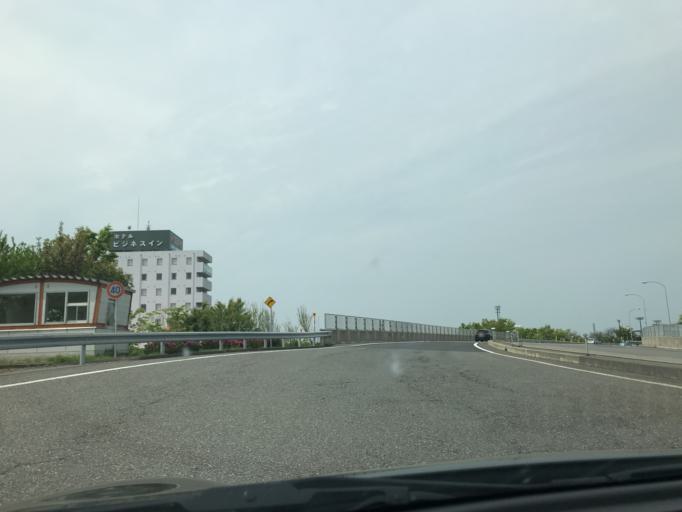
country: JP
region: Niigata
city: Kameda-honcho
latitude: 37.8775
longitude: 139.0788
